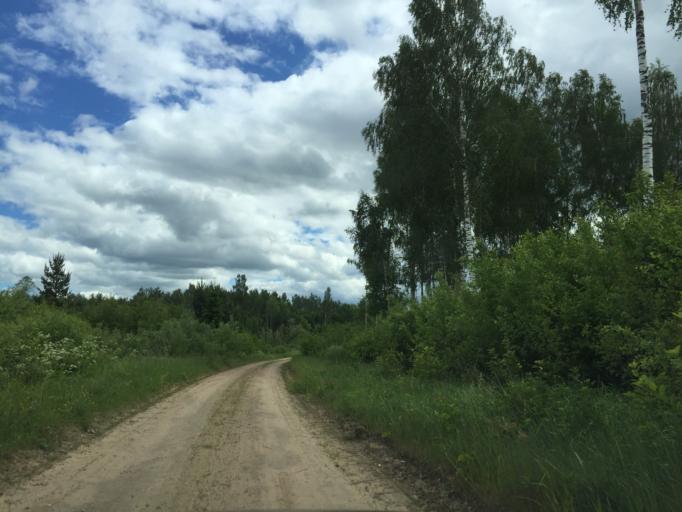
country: LV
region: Lecava
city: Iecava
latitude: 56.5662
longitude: 24.3057
